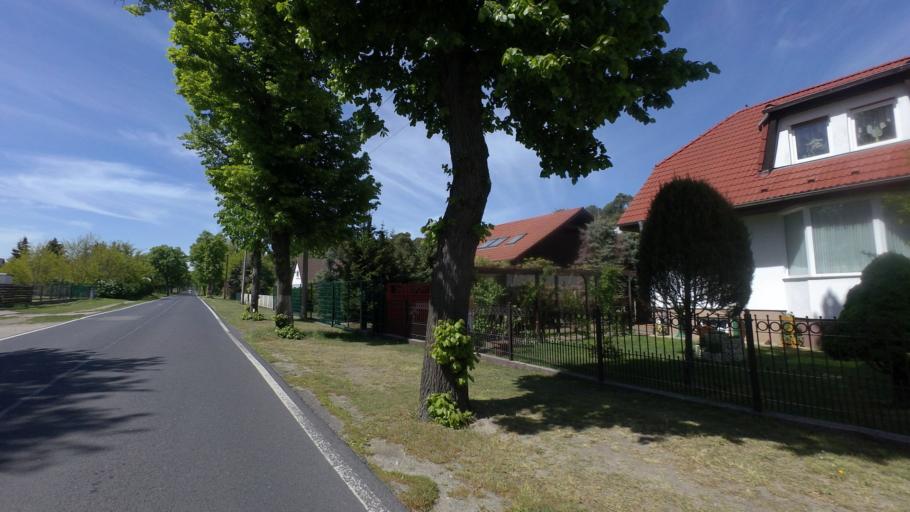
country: DE
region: Brandenburg
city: Baruth
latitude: 52.0617
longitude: 13.5006
